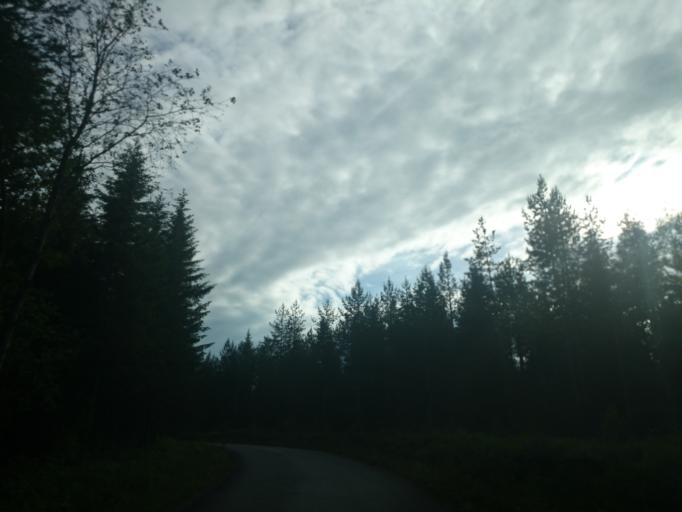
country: SE
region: Vaesternorrland
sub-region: Haernoesands Kommun
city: Haernoesand
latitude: 62.5858
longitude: 17.9060
